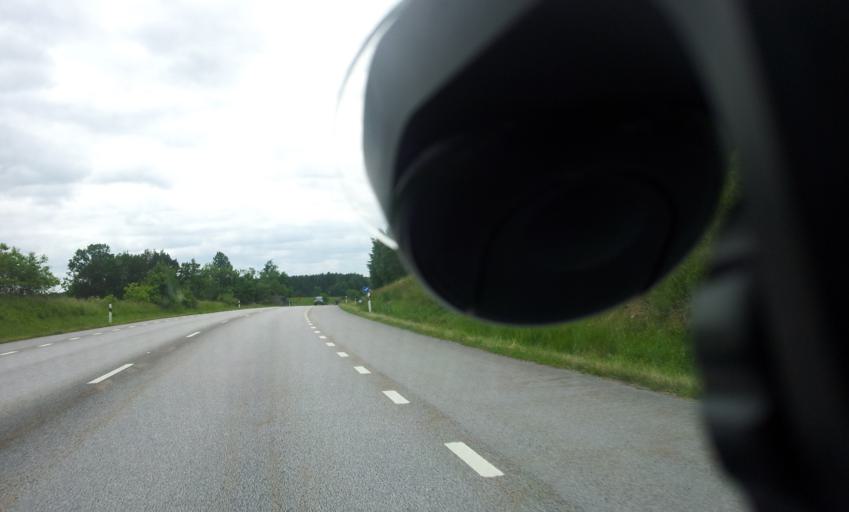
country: SE
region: Kalmar
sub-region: Vasterviks Kommun
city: Ankarsrum
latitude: 57.7142
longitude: 16.4502
